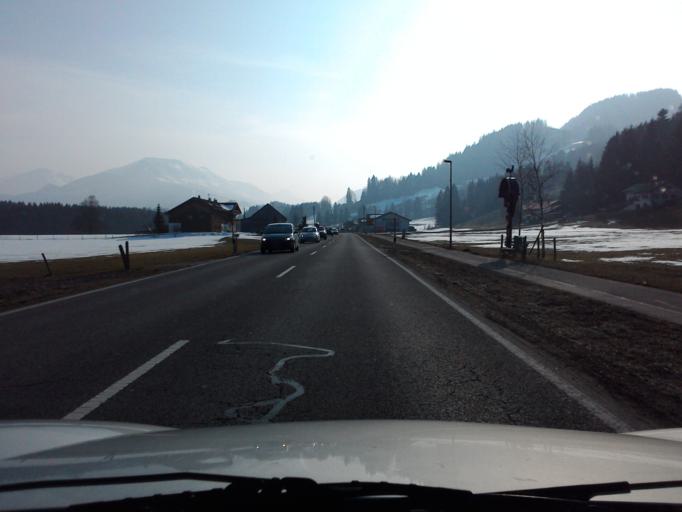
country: DE
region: Bavaria
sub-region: Swabia
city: Oberstdorf
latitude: 47.4345
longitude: 10.2727
